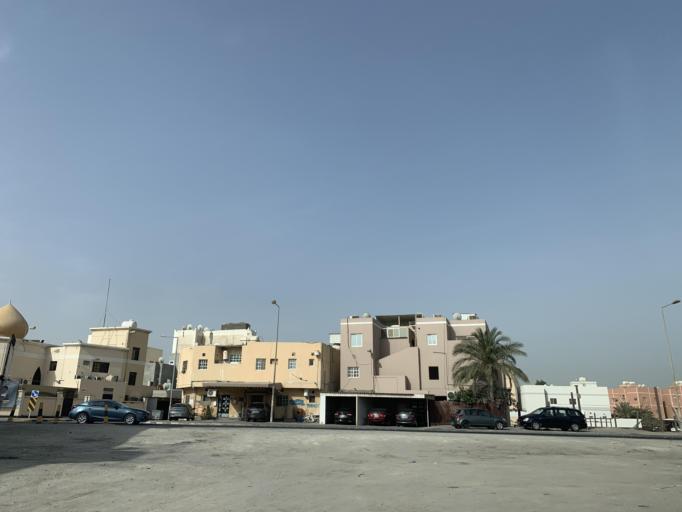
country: BH
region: Northern
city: Madinat `Isa
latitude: 26.1805
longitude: 50.5610
